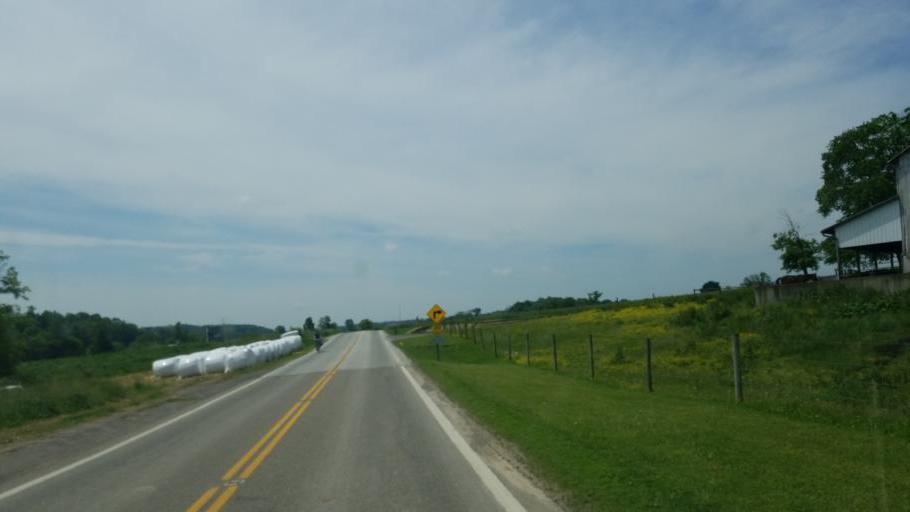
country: US
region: Ohio
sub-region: Tuscarawas County
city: Sugarcreek
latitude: 40.4716
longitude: -81.6837
